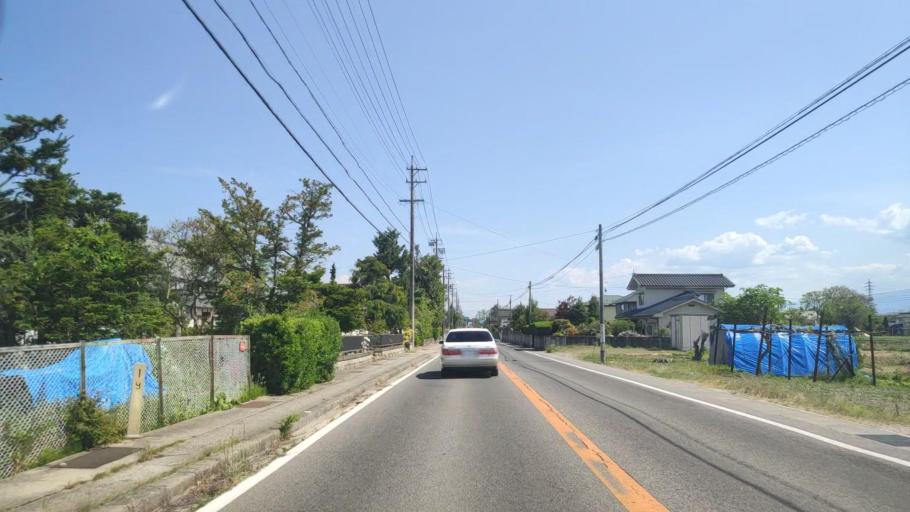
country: JP
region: Nagano
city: Hotaka
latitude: 36.3573
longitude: 137.8799
